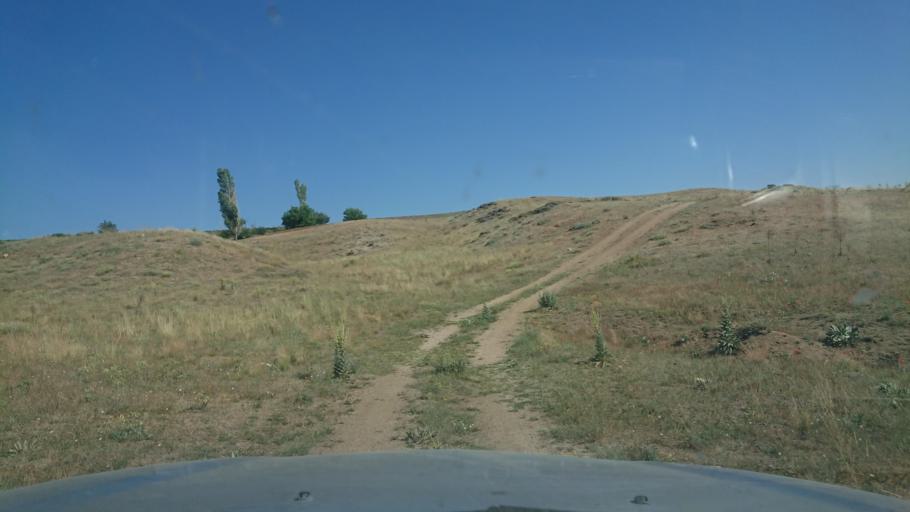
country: TR
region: Aksaray
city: Agacoren
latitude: 38.8457
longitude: 33.9265
